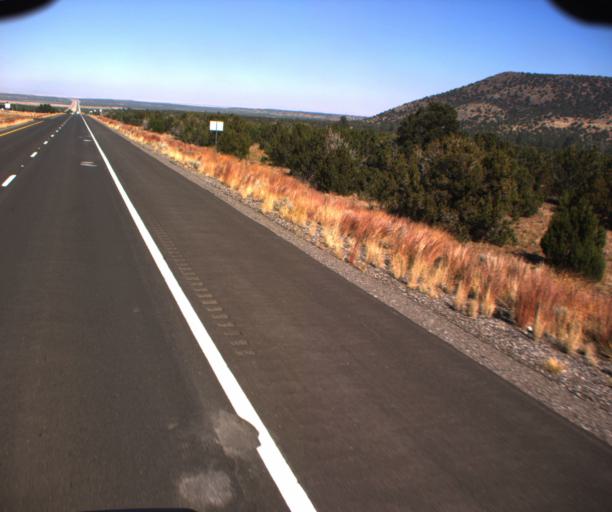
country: US
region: Arizona
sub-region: Coconino County
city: Flagstaff
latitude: 35.4039
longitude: -111.5750
